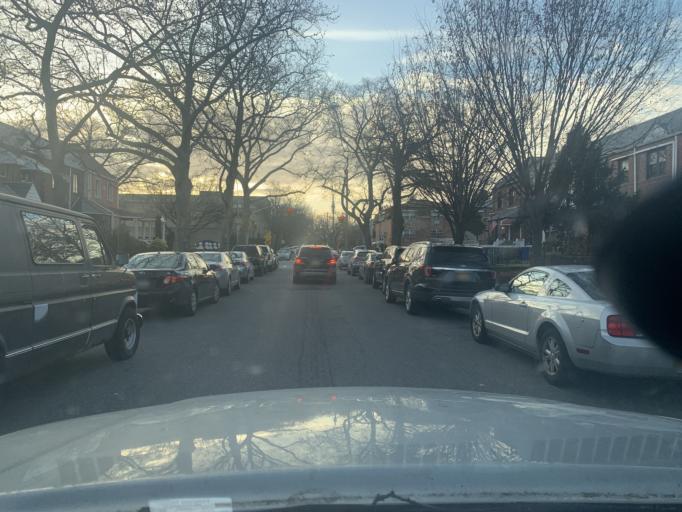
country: US
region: New York
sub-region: Kings County
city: East New York
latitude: 40.7218
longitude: -73.8877
